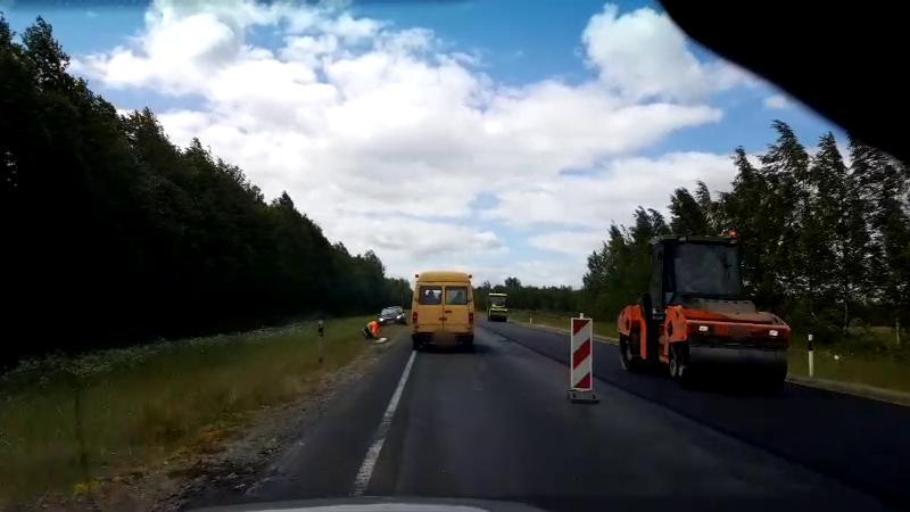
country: LV
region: Salacgrivas
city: Ainazi
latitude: 57.9962
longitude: 24.4753
